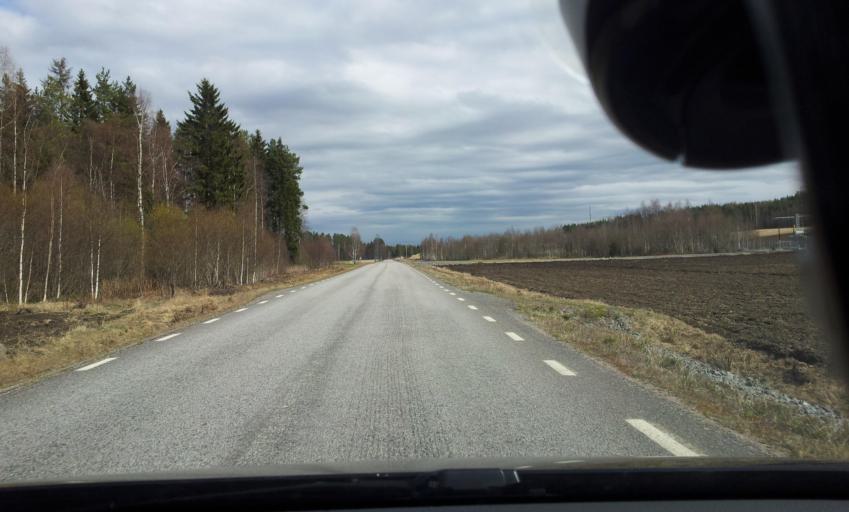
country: SE
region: Gaevleborg
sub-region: Ljusdals Kommun
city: Ljusdal
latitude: 61.7682
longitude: 16.0019
